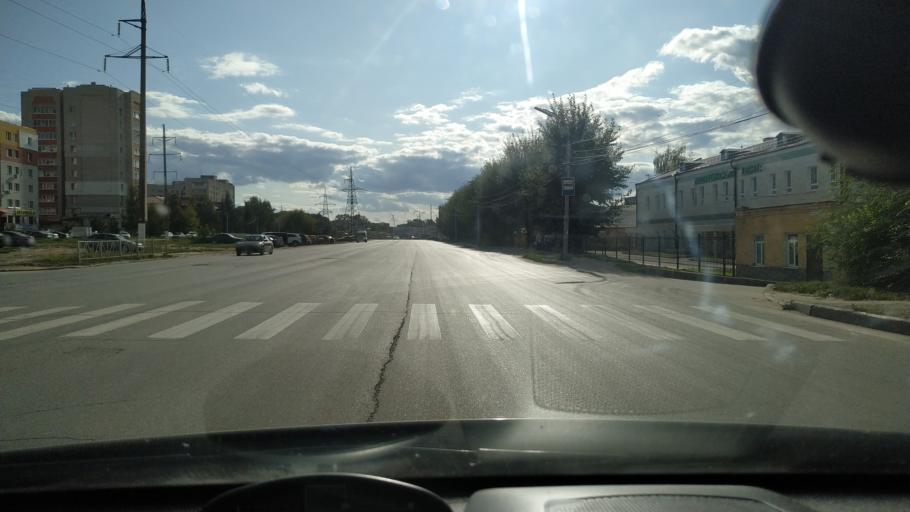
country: RU
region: Rjazan
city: Ryazan'
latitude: 54.6191
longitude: 39.6978
